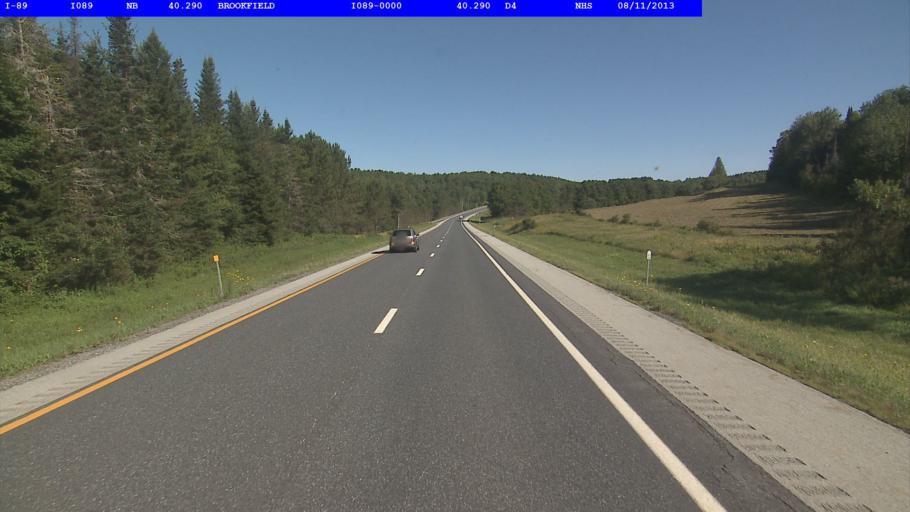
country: US
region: Vermont
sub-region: Orange County
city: Williamstown
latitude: 44.0776
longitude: -72.6113
